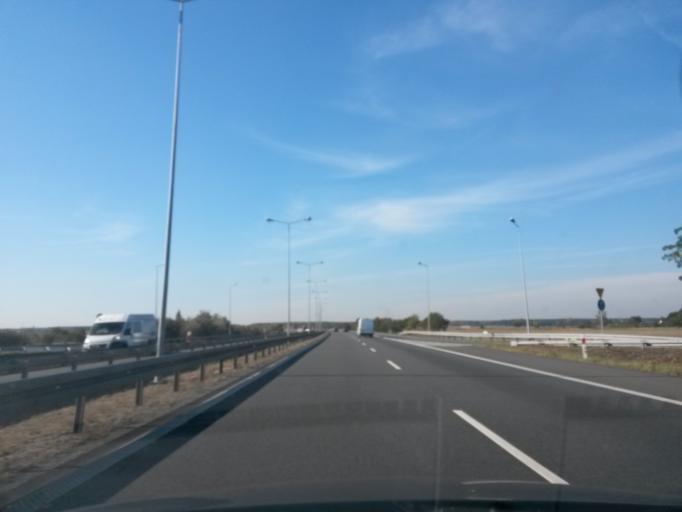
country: PL
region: Opole Voivodeship
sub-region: Powiat opolski
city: Proszkow
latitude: 50.5698
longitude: 17.8597
